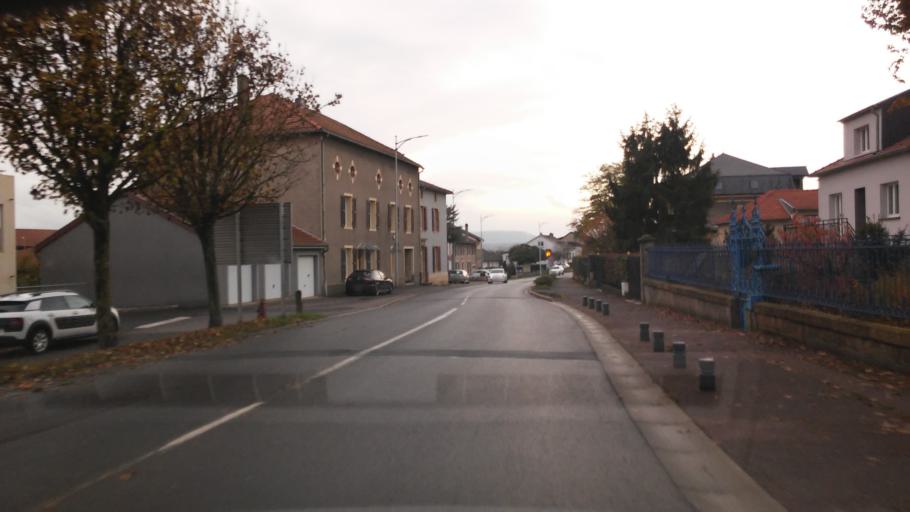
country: FR
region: Lorraine
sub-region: Departement de la Moselle
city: Ay-sur-Moselle
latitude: 49.2445
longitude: 6.2103
